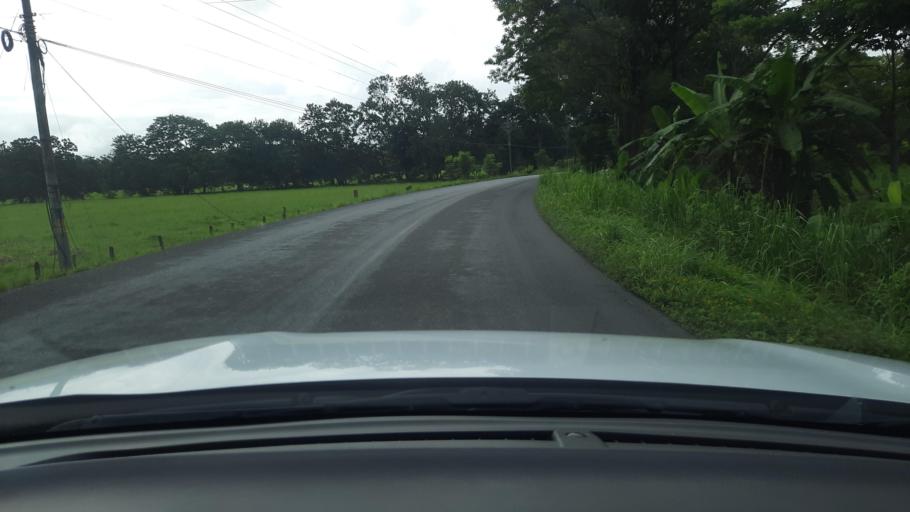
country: CR
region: Alajuela
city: San Jose
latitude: 10.9280
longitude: -85.0930
